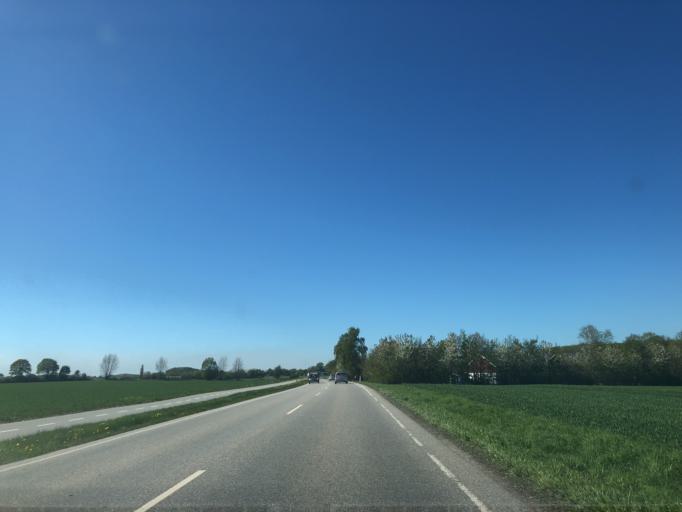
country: DK
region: Zealand
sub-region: Stevns Kommune
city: Store Heddinge
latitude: 55.3370
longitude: 12.3488
